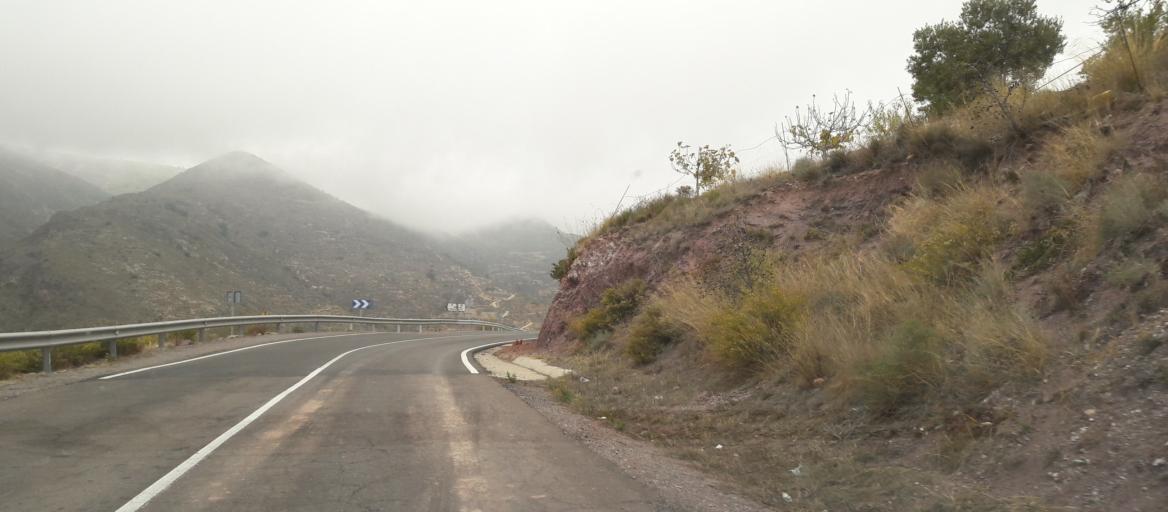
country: ES
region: Andalusia
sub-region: Provincia de Almeria
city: Enix
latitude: 36.8849
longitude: -2.6259
